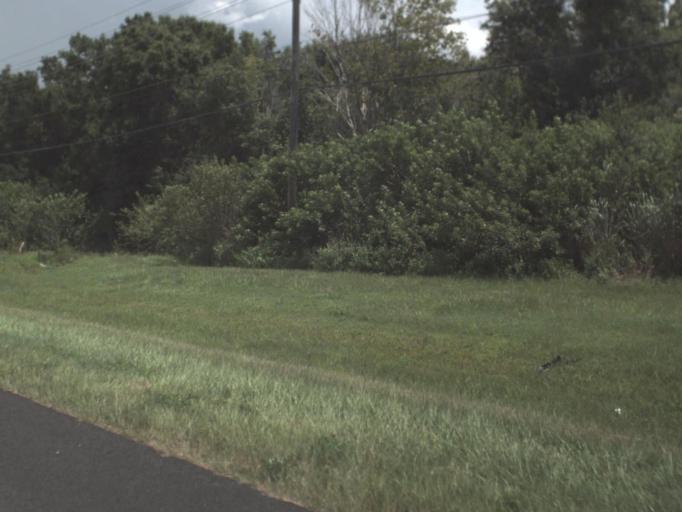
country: US
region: Florida
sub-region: Hillsborough County
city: Sun City Center
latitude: 27.7669
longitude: -82.3349
